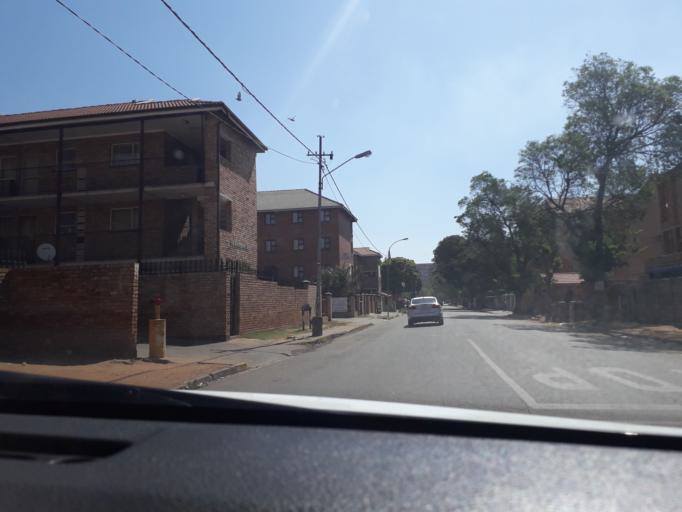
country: ZA
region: Gauteng
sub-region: City of Johannesburg Metropolitan Municipality
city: Modderfontein
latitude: -26.1042
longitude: 28.2351
